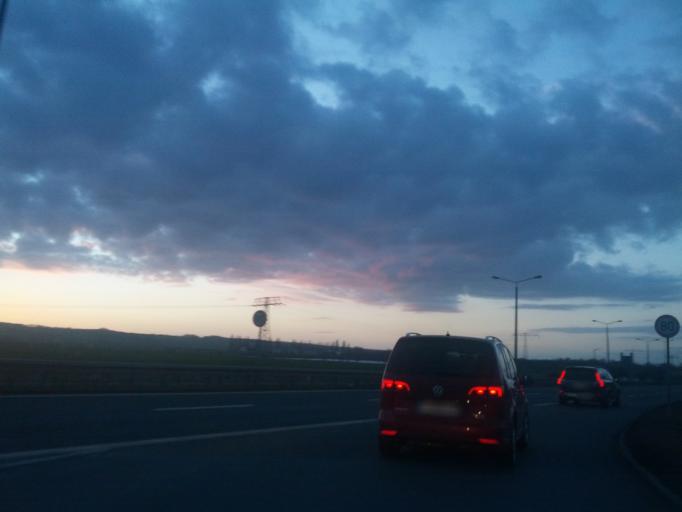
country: DE
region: Thuringia
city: Erfurt
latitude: 51.0048
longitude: 10.9947
